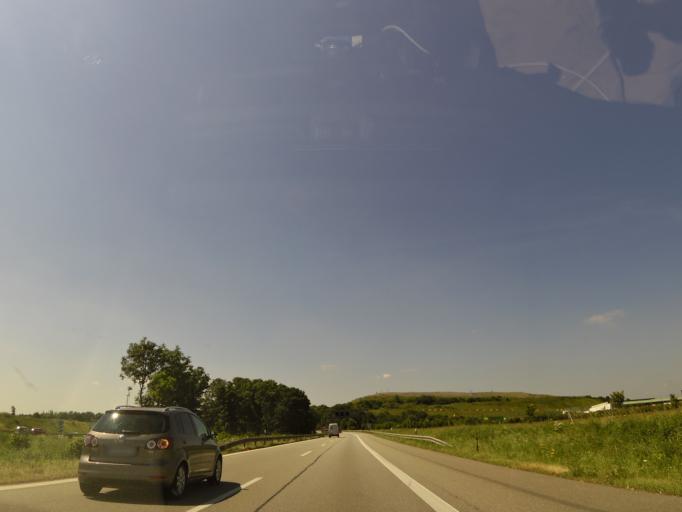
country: DE
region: Bavaria
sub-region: Upper Bavaria
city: Garching bei Munchen
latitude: 48.2300
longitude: 11.6332
